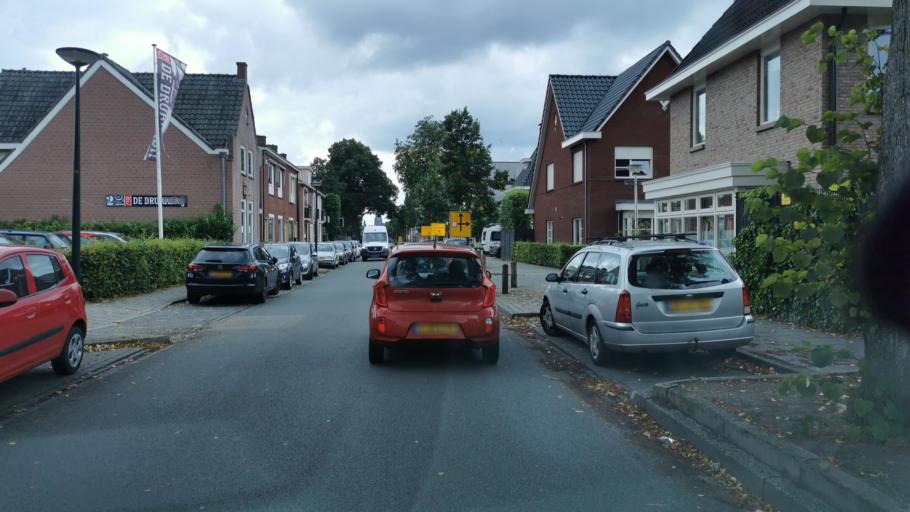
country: NL
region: Overijssel
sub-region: Gemeente Enschede
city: Enschede
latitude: 52.2352
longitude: 6.9000
